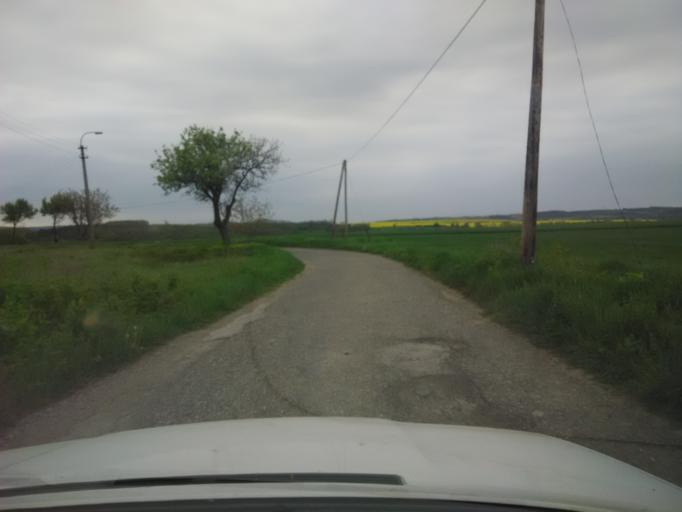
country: SK
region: Nitriansky
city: Levice
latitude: 48.2853
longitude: 18.6988
